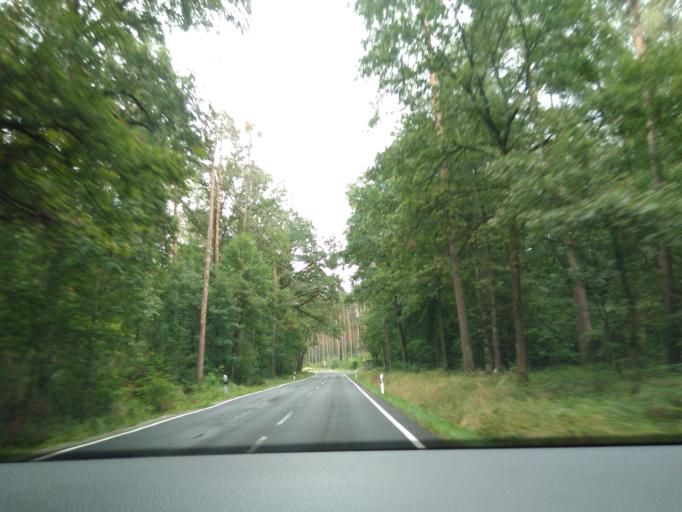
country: DE
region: Bavaria
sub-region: Regierungsbezirk Mittelfranken
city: Weisendorf
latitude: 49.6521
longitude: 10.8102
